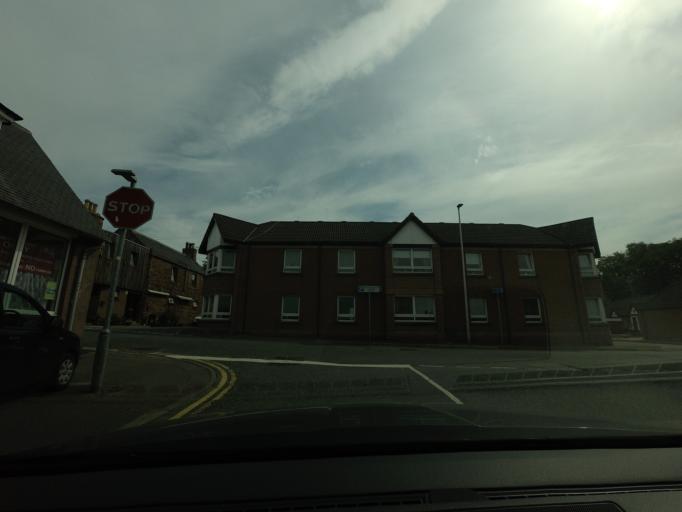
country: GB
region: Scotland
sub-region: Aberdeenshire
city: Turriff
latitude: 57.5378
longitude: -2.4557
